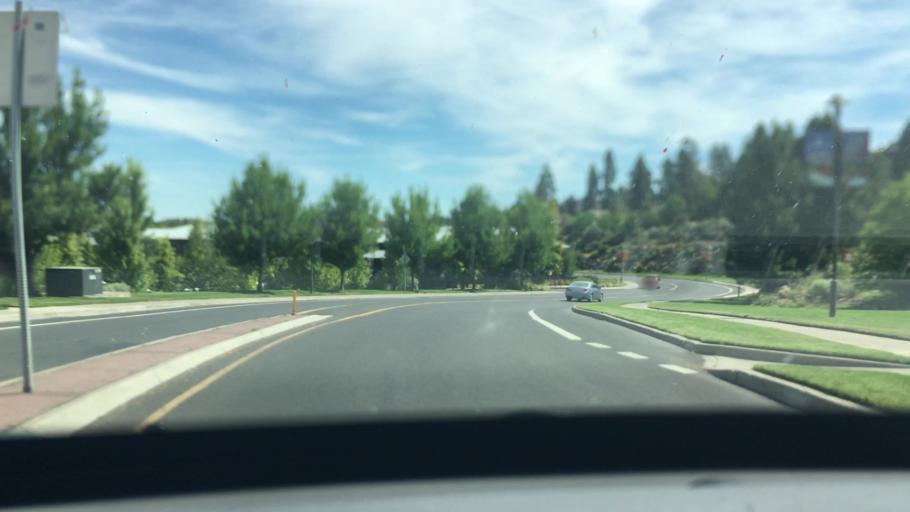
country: US
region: Oregon
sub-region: Deschutes County
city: Bend
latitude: 44.0408
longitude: -121.3163
